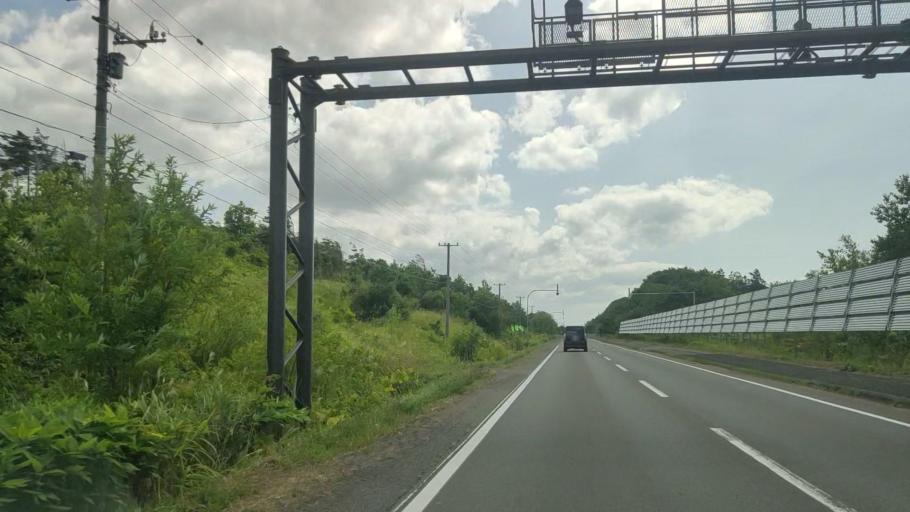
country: JP
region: Hokkaido
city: Makubetsu
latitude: 44.7683
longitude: 141.7929
